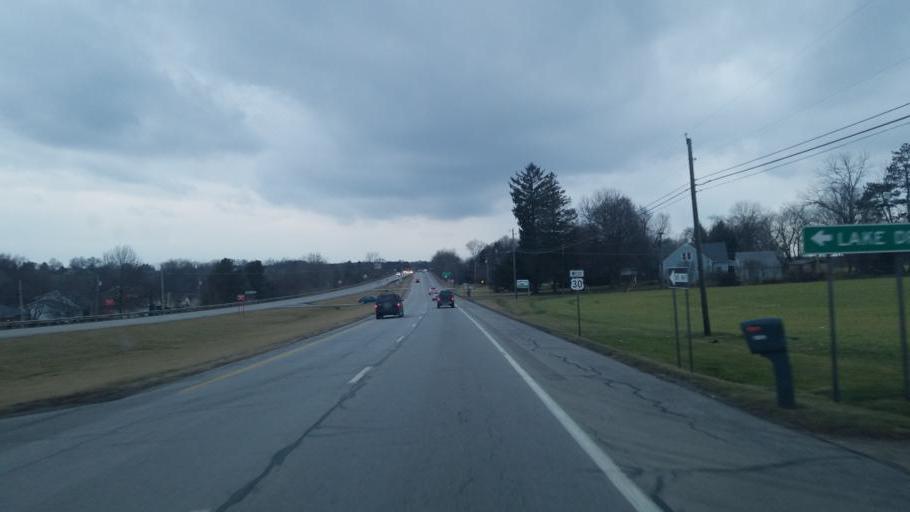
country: US
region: Ohio
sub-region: Wayne County
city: Dalton
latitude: 40.7998
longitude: -81.7361
